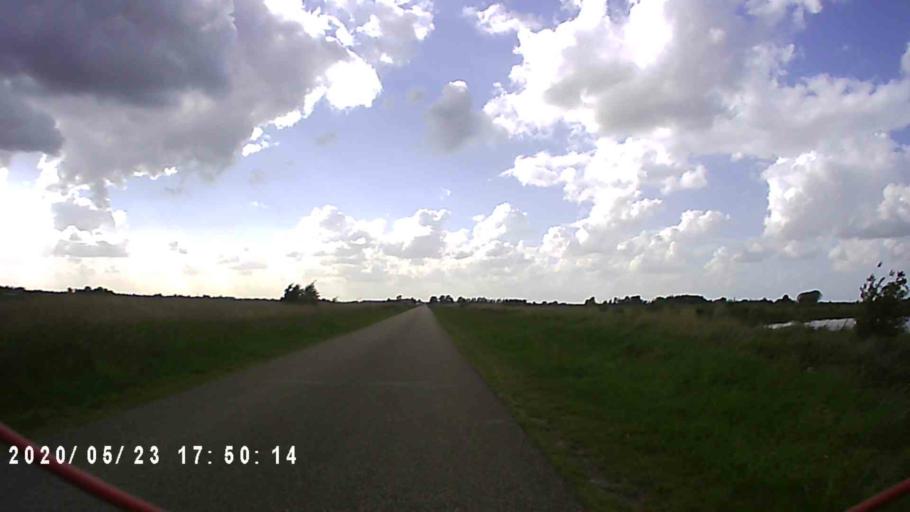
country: NL
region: Groningen
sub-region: Gemeente Slochteren
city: Slochteren
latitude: 53.2389
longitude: 6.7665
